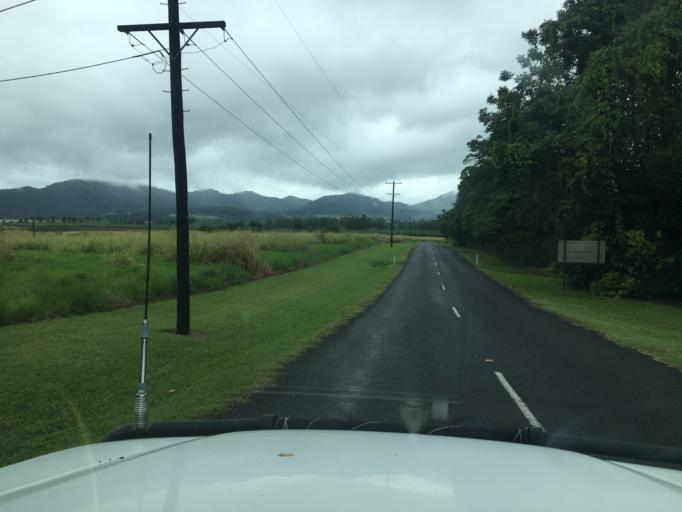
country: AU
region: Queensland
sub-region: Cassowary Coast
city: Innisfail
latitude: -17.4388
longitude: 145.8602
